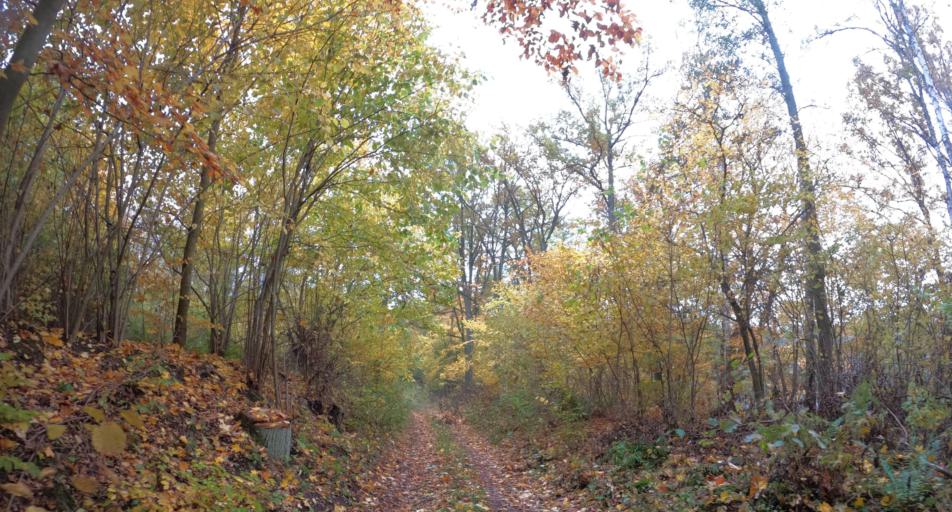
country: PL
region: West Pomeranian Voivodeship
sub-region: Powiat lobeski
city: Wegorzyno
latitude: 53.5238
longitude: 15.6676
